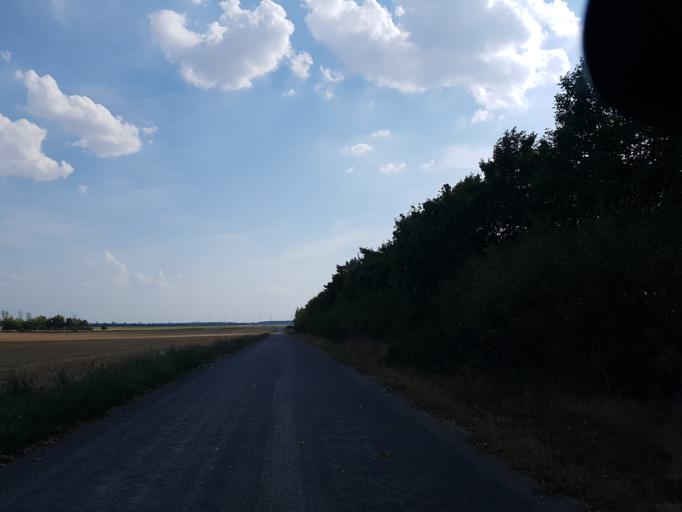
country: DE
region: Brandenburg
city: Treuenbrietzen
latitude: 51.9941
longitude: 12.8688
